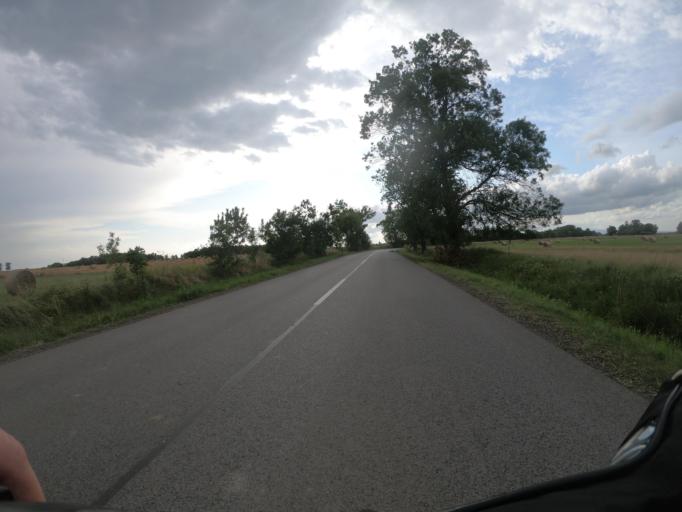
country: HU
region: Borsod-Abauj-Zemplen
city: Mezocsat
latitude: 47.8214
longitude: 20.8542
